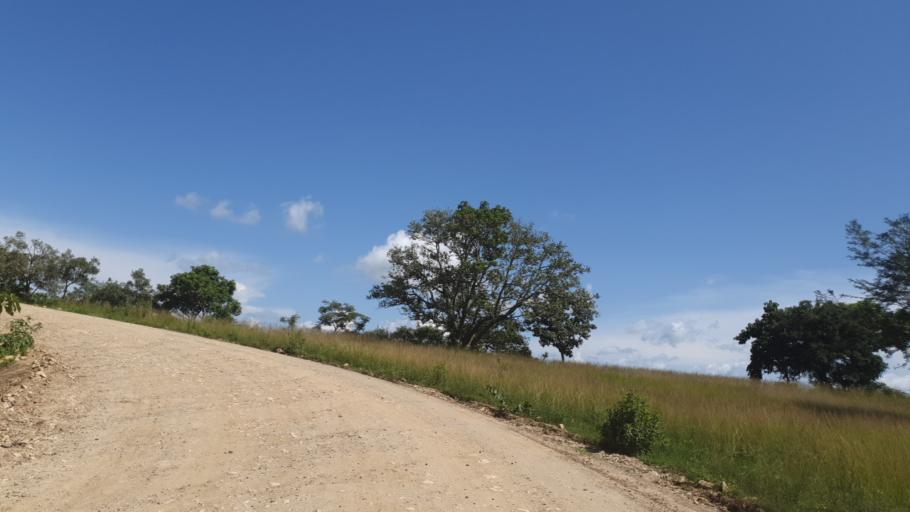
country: ET
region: Oromiya
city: Shambu
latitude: 9.7108
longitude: 36.6278
